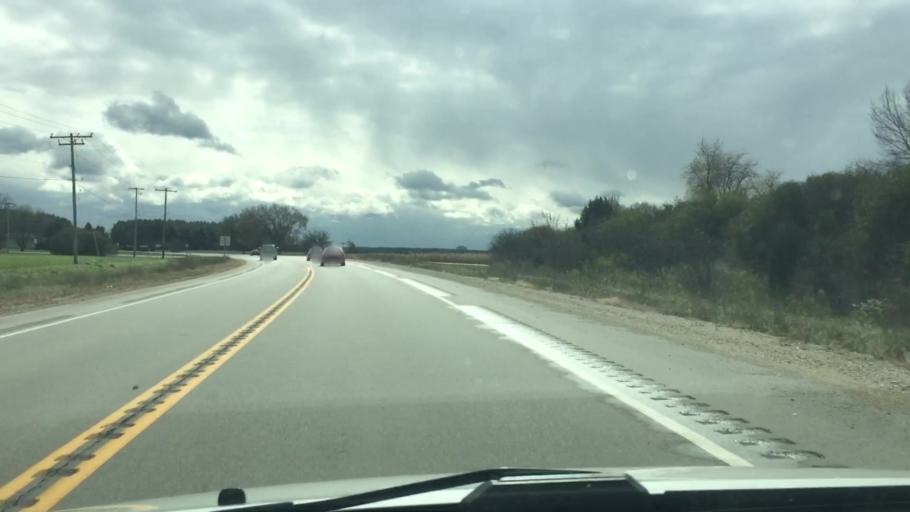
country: US
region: Wisconsin
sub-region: Waukesha County
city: Dousman
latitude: 43.0487
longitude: -88.4709
